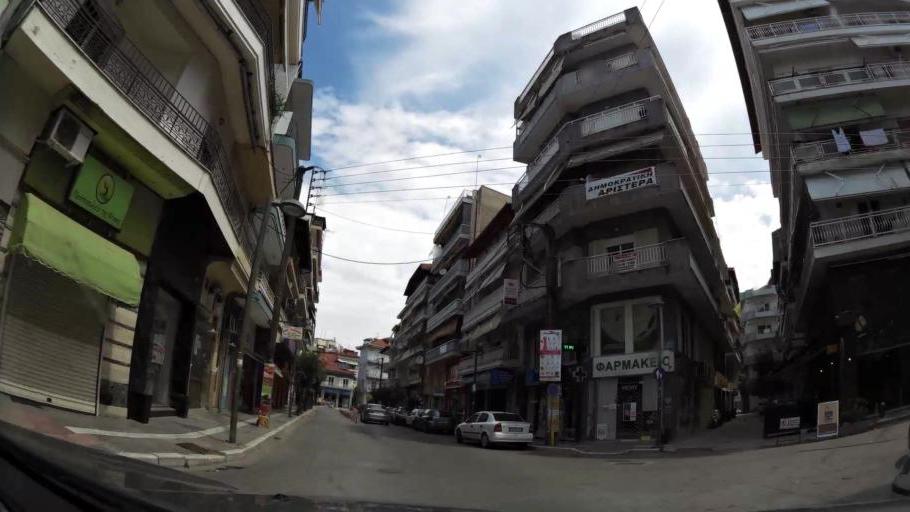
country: GR
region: Central Macedonia
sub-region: Nomos Pierias
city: Katerini
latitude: 40.2725
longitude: 22.5091
